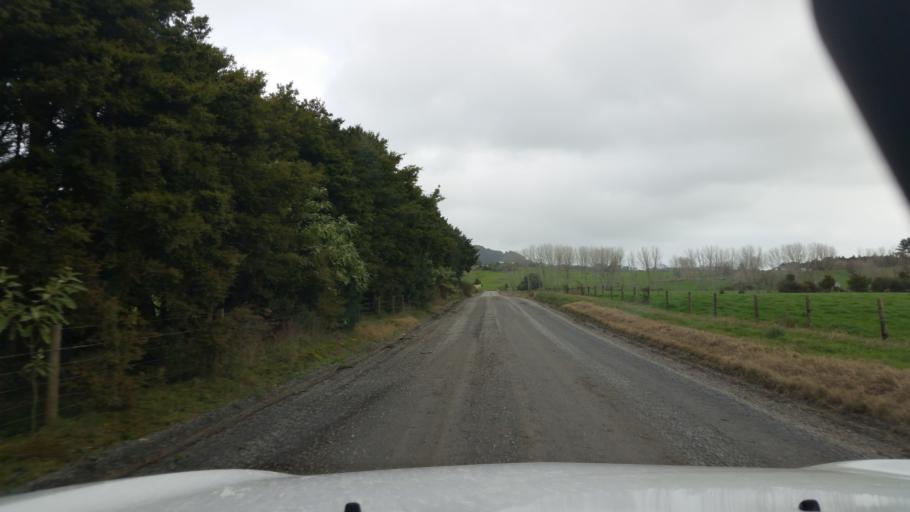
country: NZ
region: Northland
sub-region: Whangarei
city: Maungatapere
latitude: -35.6249
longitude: 174.1972
